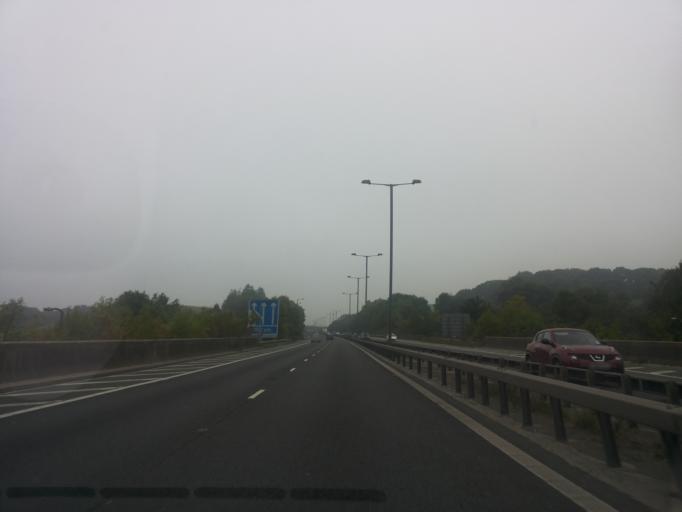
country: GB
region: England
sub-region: Borough of Bury
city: Bury
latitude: 53.6054
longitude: -2.2753
